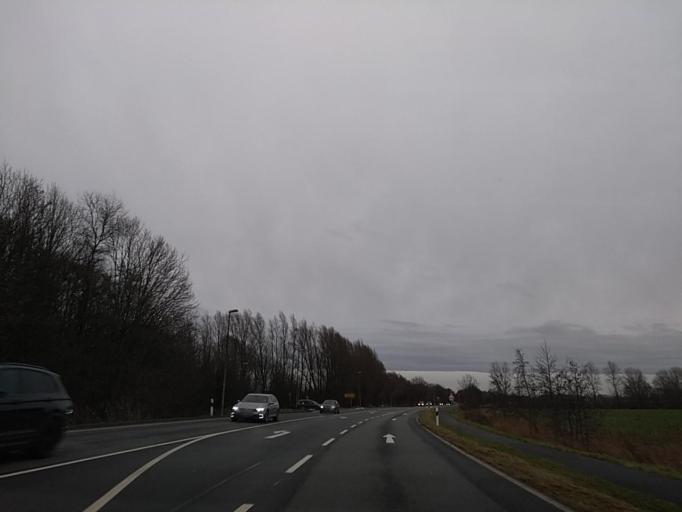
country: DE
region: Lower Saxony
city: Emden
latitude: 53.3615
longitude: 7.1387
